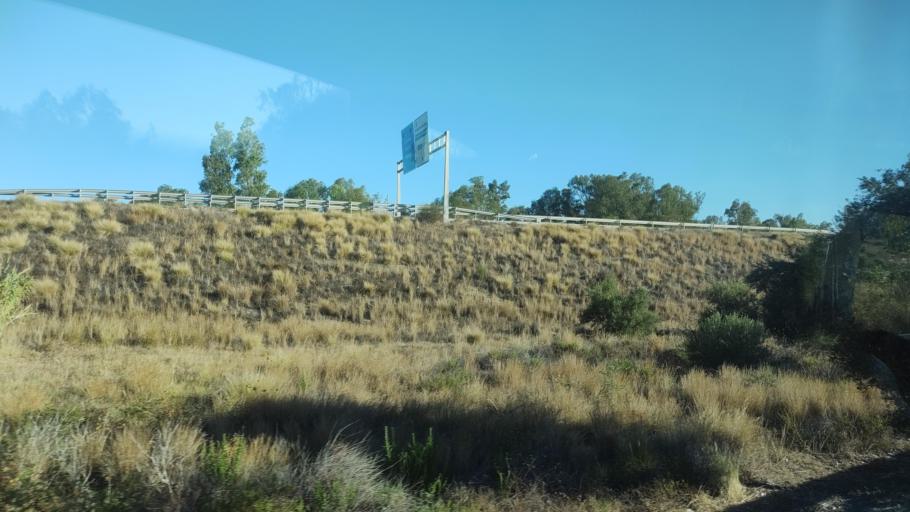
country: ES
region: Andalusia
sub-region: Provincia de Malaga
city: Torremolinos
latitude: 36.6491
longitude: -4.4816
